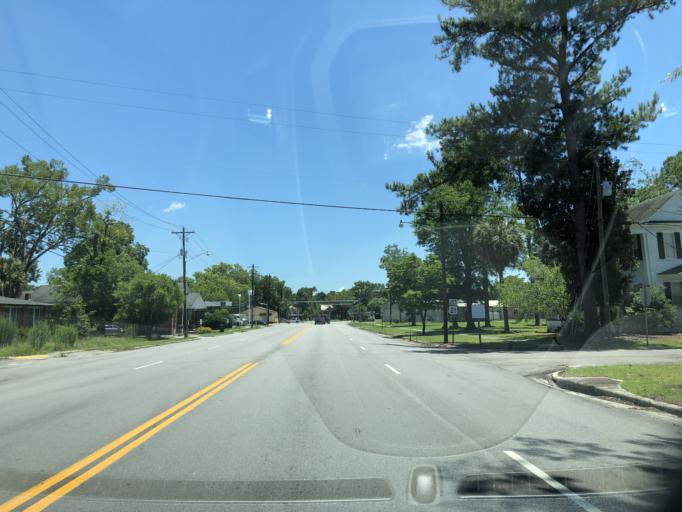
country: US
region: South Carolina
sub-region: Orangeburg County
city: Branchville
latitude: 33.2501
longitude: -80.8181
